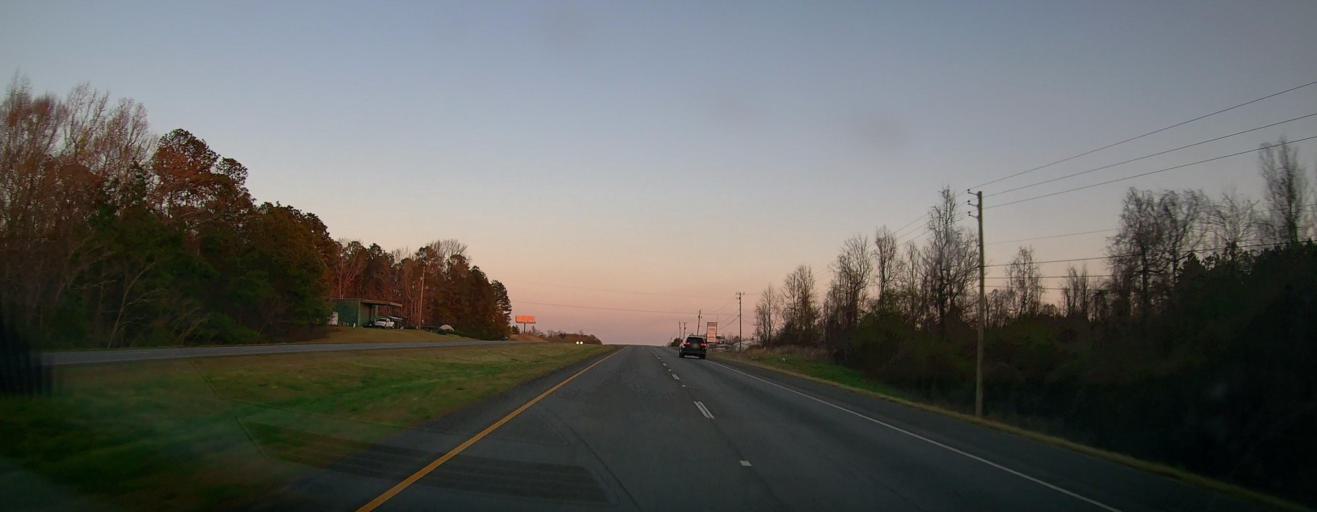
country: US
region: Alabama
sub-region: Tallapoosa County
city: Alexander City
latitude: 32.9569
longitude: -85.9982
